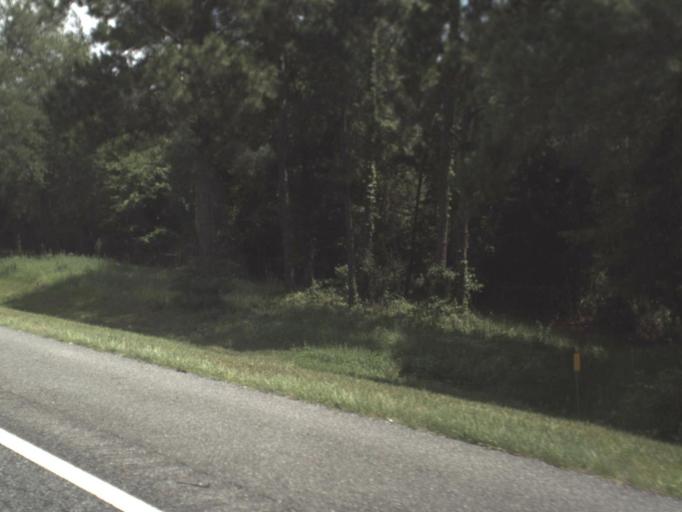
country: US
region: Florida
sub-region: Columbia County
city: Five Points
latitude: 30.2150
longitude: -82.7064
